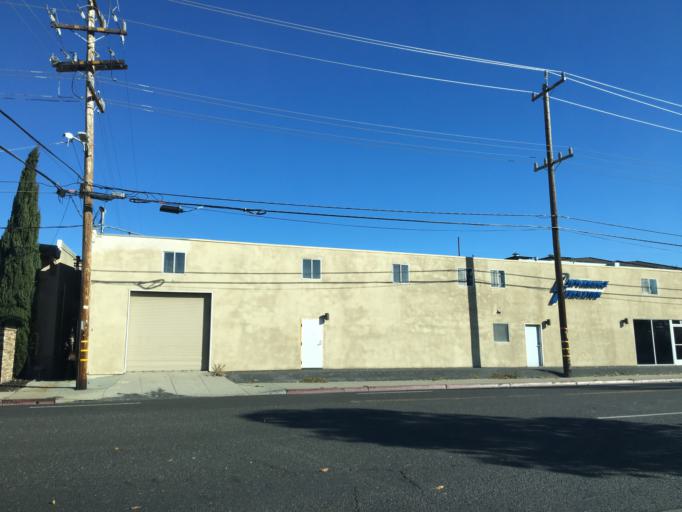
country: US
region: California
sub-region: San Mateo County
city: Redwood City
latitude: 37.4986
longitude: -122.2419
